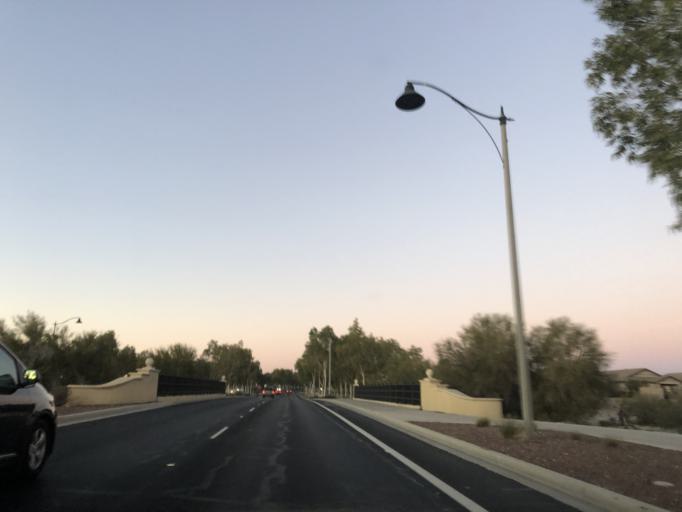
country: US
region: Arizona
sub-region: Maricopa County
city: Citrus Park
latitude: 33.4682
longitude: -112.5042
